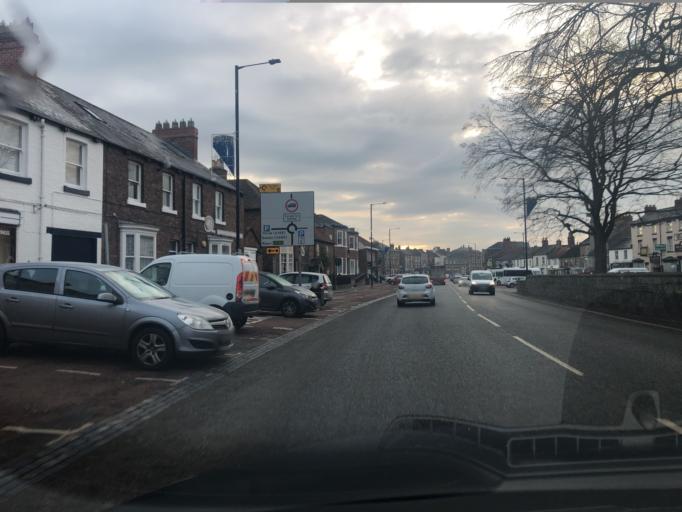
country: GB
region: England
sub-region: North Yorkshire
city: Northallerton
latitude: 54.3425
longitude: -1.4363
